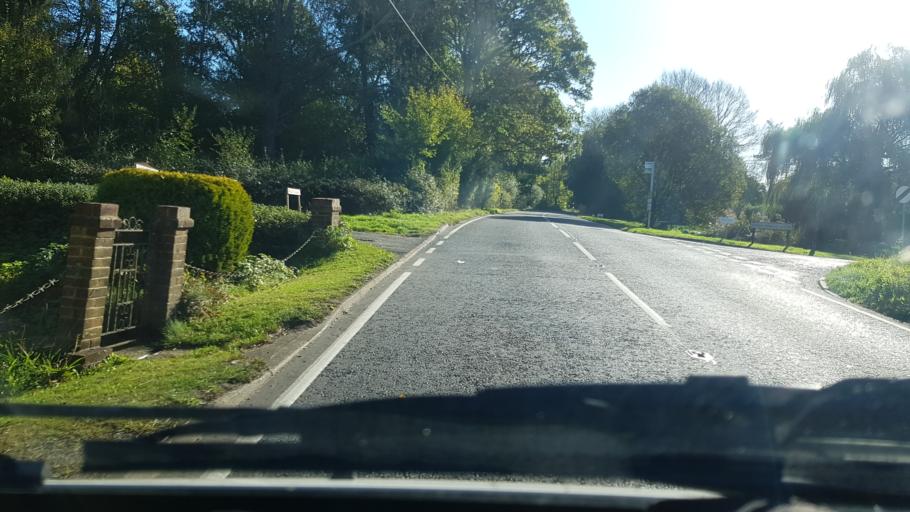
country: GB
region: England
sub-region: Surrey
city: Cranleigh
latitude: 51.1741
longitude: -0.5154
